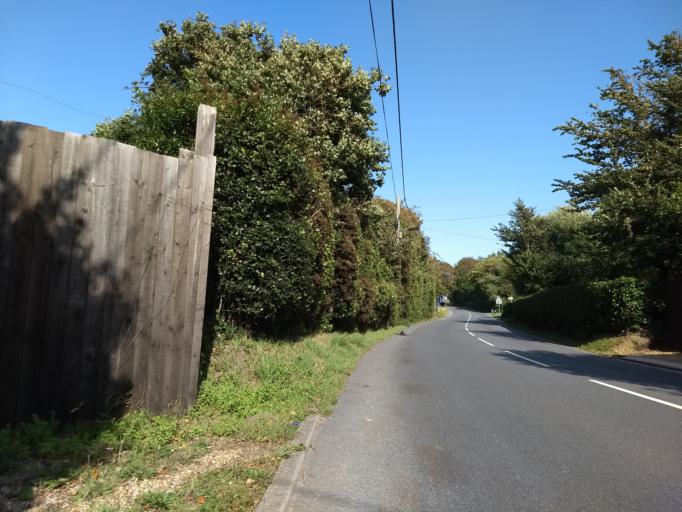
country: GB
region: England
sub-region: Isle of Wight
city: Totland
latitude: 50.6907
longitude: -1.5294
